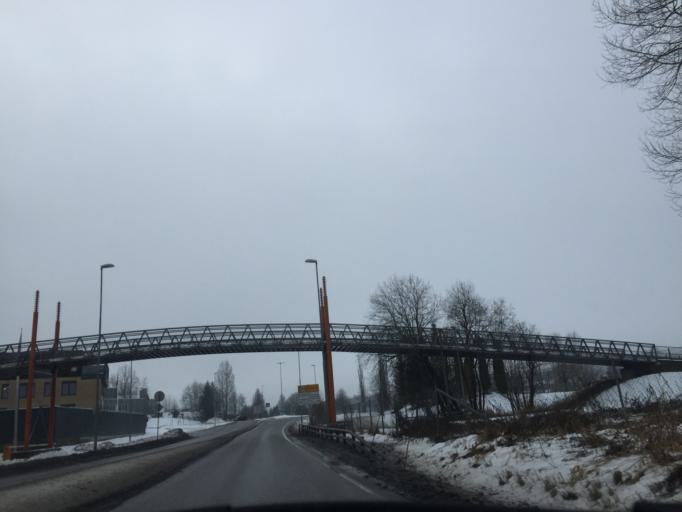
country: NO
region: Akershus
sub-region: Frogn
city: Drobak
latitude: 59.6751
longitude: 10.6570
